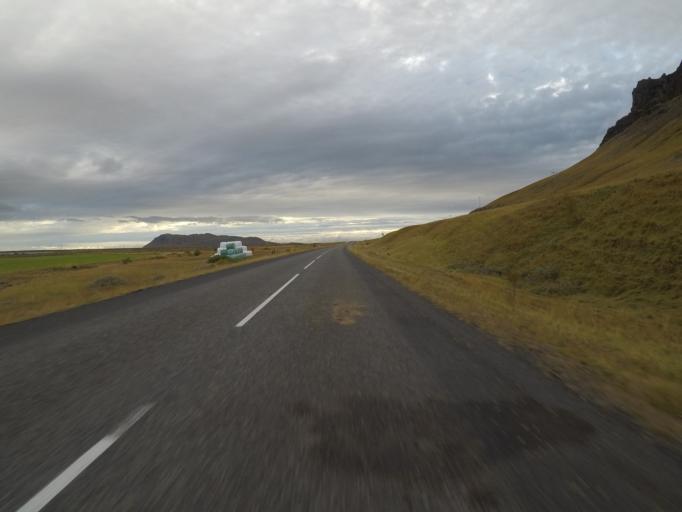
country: IS
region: South
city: Vestmannaeyjar
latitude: 64.0709
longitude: -20.0416
